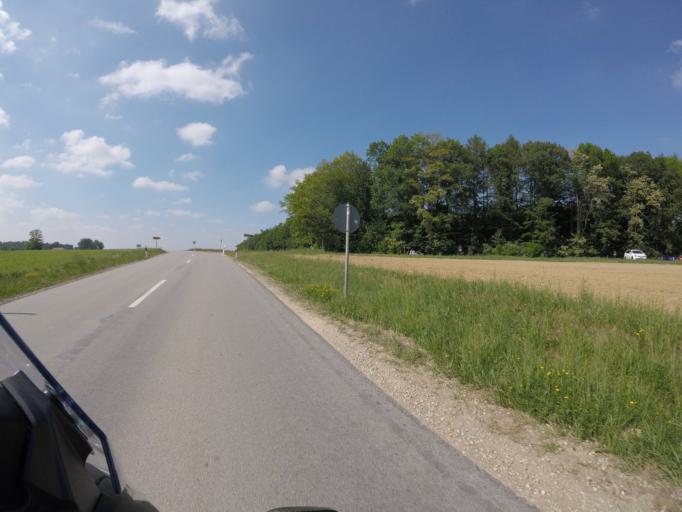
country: DE
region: Bavaria
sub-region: Upper Bavaria
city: Jetzendorf
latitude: 48.4404
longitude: 11.4164
